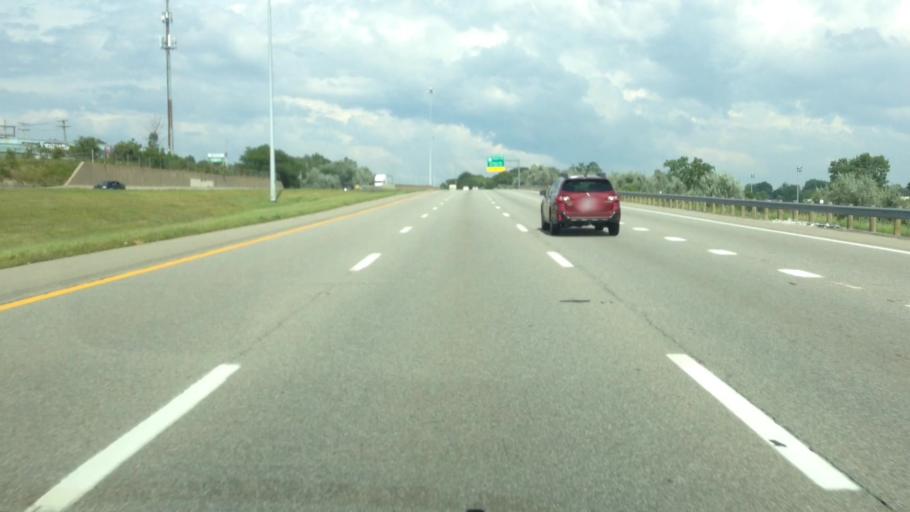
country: US
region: Ohio
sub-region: Cuyahoga County
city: Brooklyn
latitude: 41.4518
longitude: -81.7277
